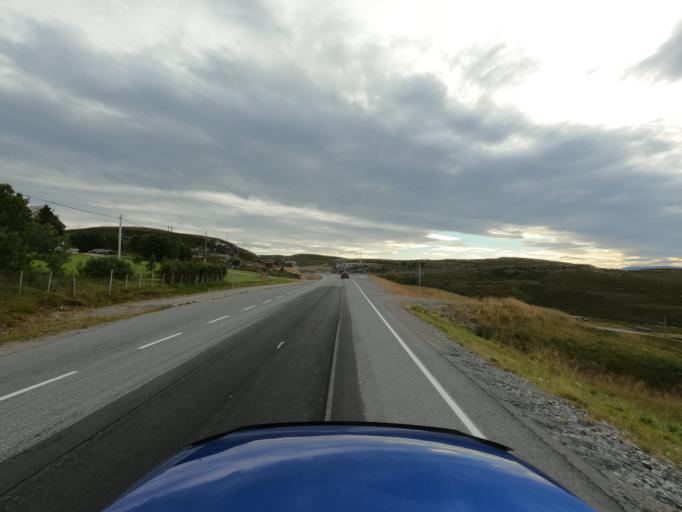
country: NO
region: Finnmark Fylke
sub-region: Hammerfest
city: Rypefjord
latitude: 70.5412
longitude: 23.7357
